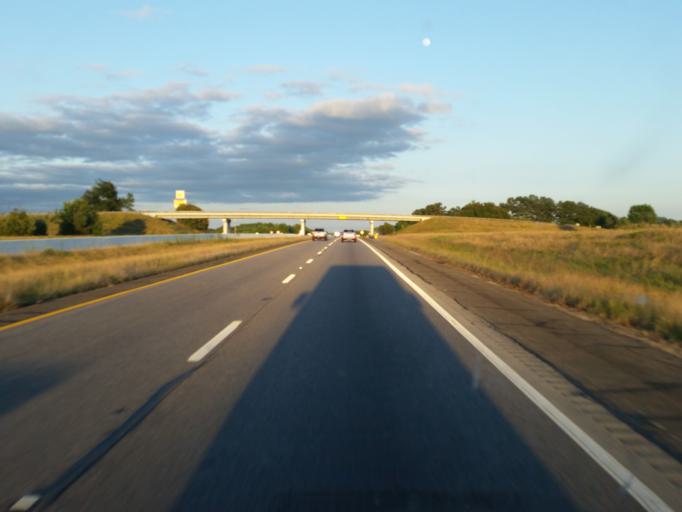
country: US
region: Texas
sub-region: Van Zandt County
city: Canton
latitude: 32.5431
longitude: -95.7595
